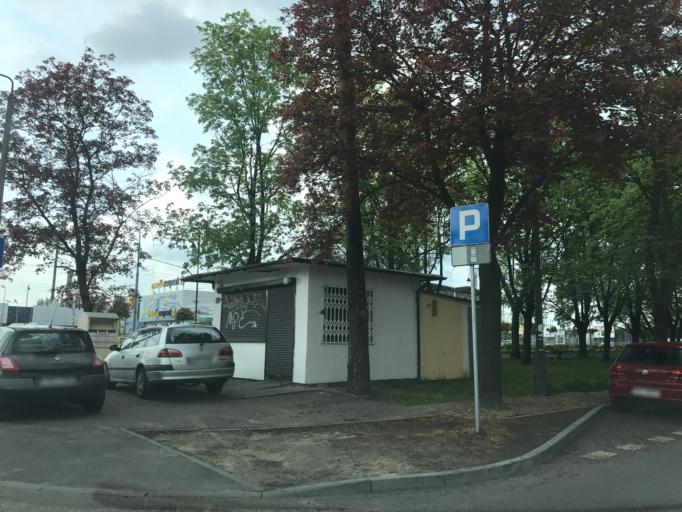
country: PL
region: Kujawsko-Pomorskie
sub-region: Bydgoszcz
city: Bydgoszcz
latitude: 53.1433
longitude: 18.0221
